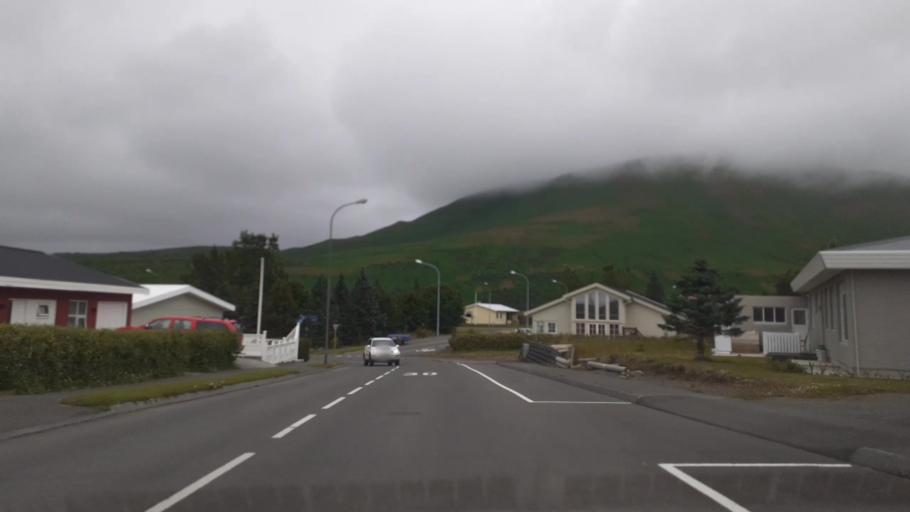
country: IS
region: Northeast
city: Husavik
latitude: 66.0385
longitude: -17.3356
